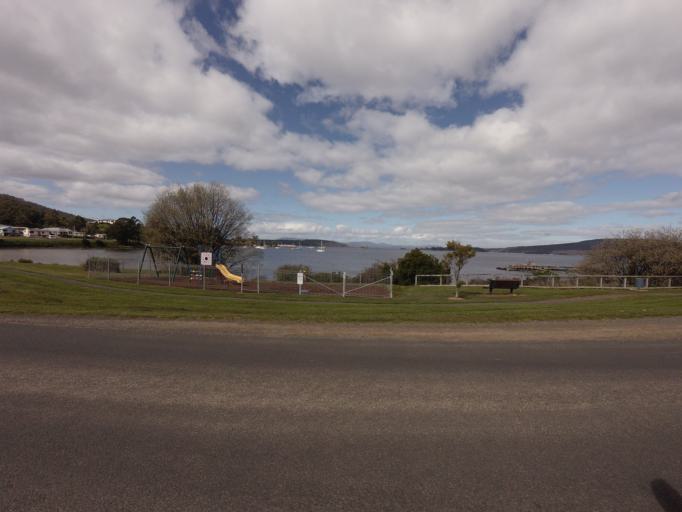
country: AU
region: Tasmania
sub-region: Huon Valley
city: Cygnet
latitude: -43.3168
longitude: 147.0111
